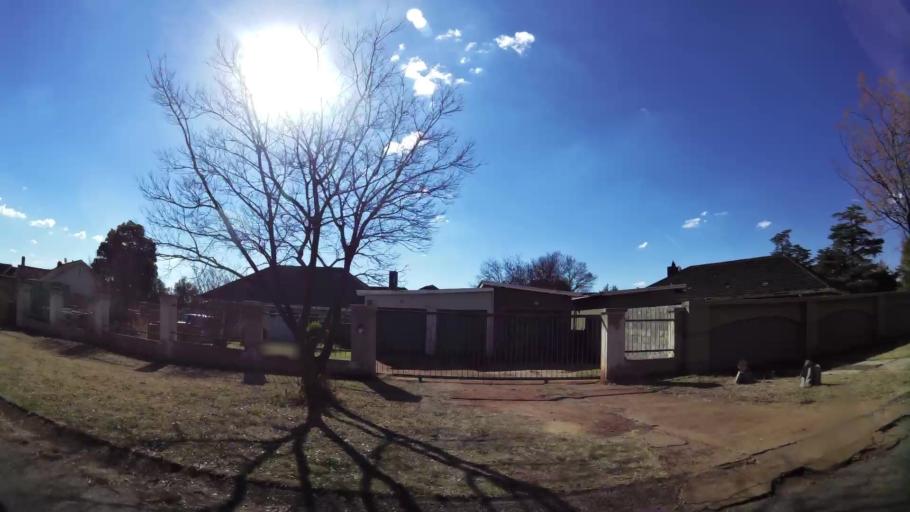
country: ZA
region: Gauteng
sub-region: West Rand District Municipality
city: Carletonville
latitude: -26.3745
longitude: 27.4038
